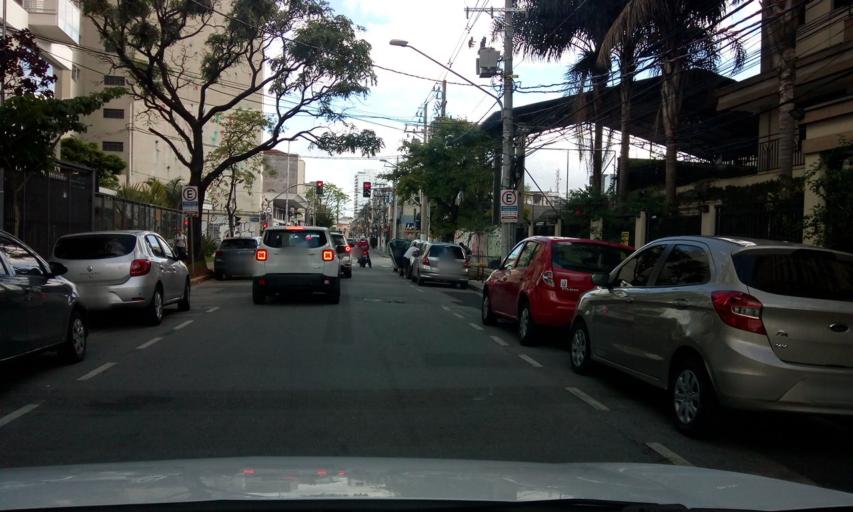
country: BR
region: Sao Paulo
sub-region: Sao Paulo
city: Sao Paulo
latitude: -23.5645
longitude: -46.6956
